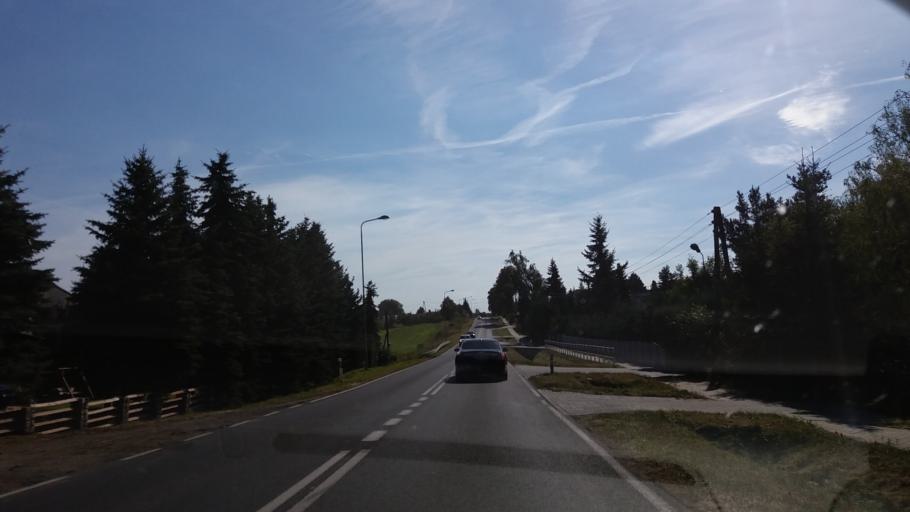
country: PL
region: Greater Poland Voivodeship
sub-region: Powiat miedzychodzki
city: Miedzychod
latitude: 52.5854
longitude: 15.8969
